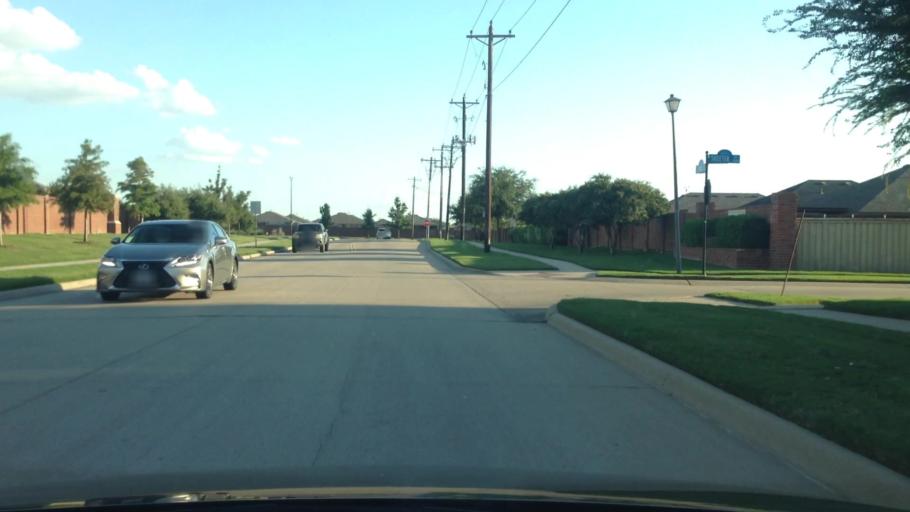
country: US
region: Texas
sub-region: Denton County
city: Little Elm
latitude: 33.1424
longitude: -96.9141
